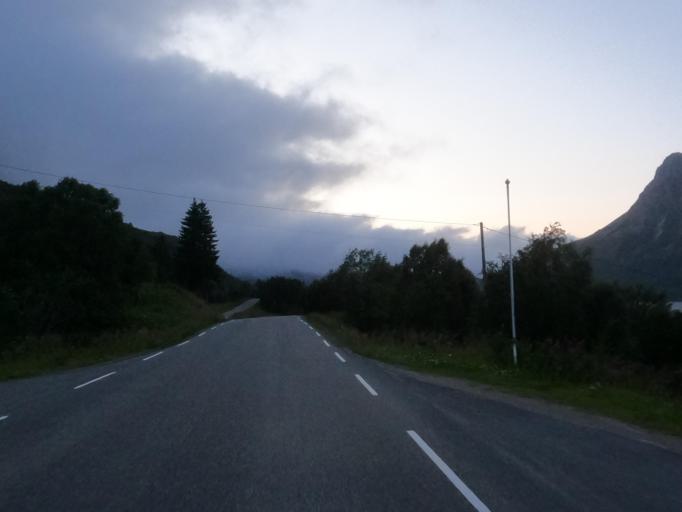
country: NO
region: Nordland
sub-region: Lodingen
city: Lodingen
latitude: 68.5846
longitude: 15.7918
